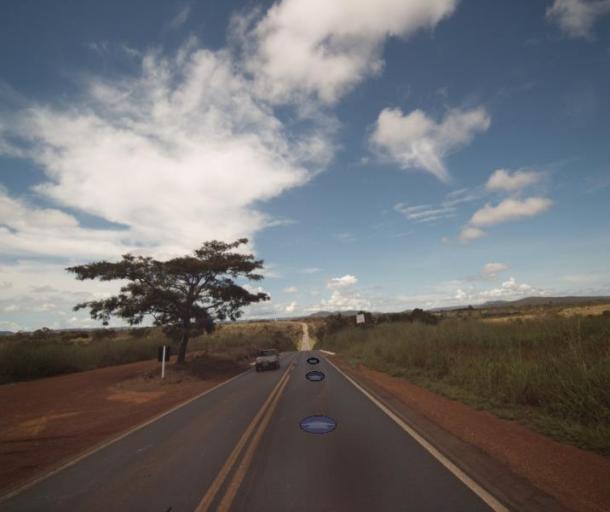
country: BR
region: Goias
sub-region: Padre Bernardo
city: Padre Bernardo
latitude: -15.3459
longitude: -48.2329
